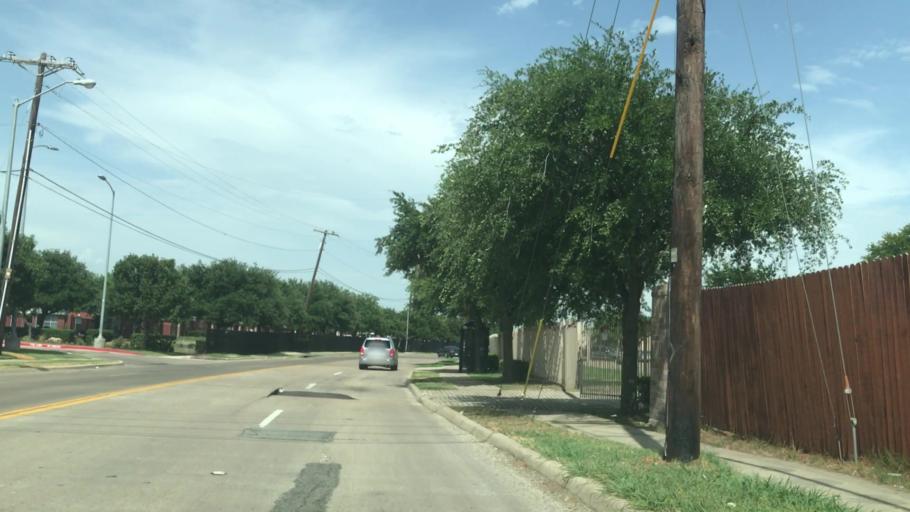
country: US
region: Texas
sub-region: Dallas County
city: Cockrell Hill
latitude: 32.7861
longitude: -96.8705
